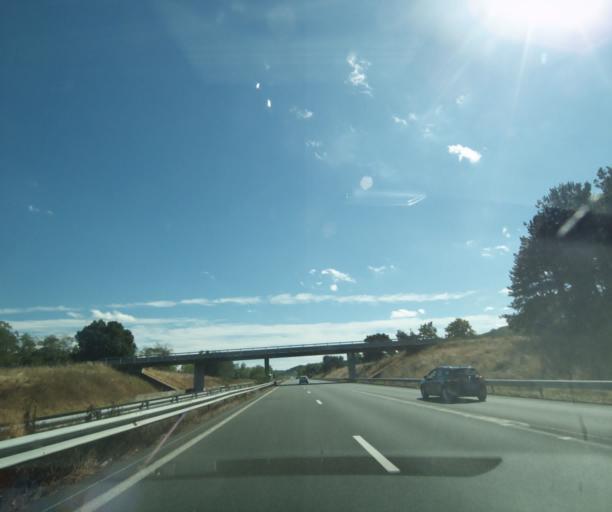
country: FR
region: Aquitaine
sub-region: Departement du Lot-et-Garonne
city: Damazan
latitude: 44.2820
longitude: 0.2684
